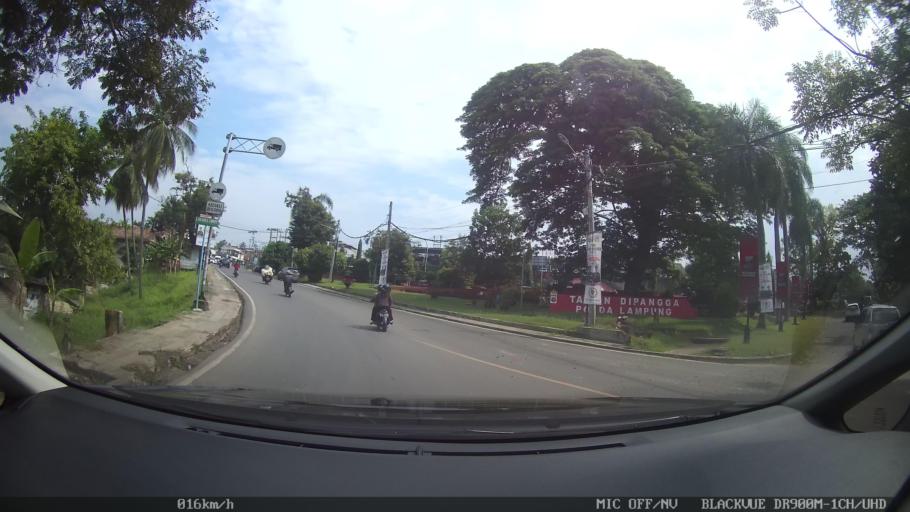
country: ID
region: Lampung
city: Bandarlampung
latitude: -5.4462
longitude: 105.2621
